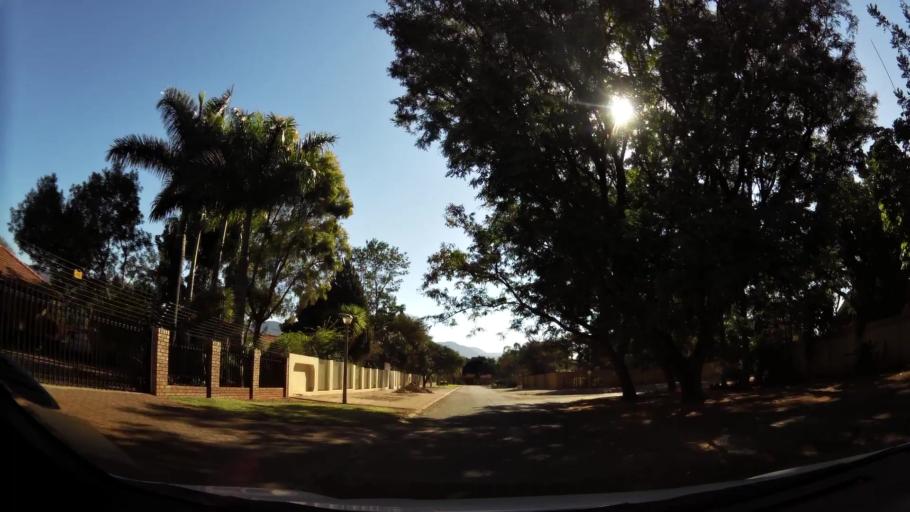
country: ZA
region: Limpopo
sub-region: Waterberg District Municipality
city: Mokopane
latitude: -24.2094
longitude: 28.9922
